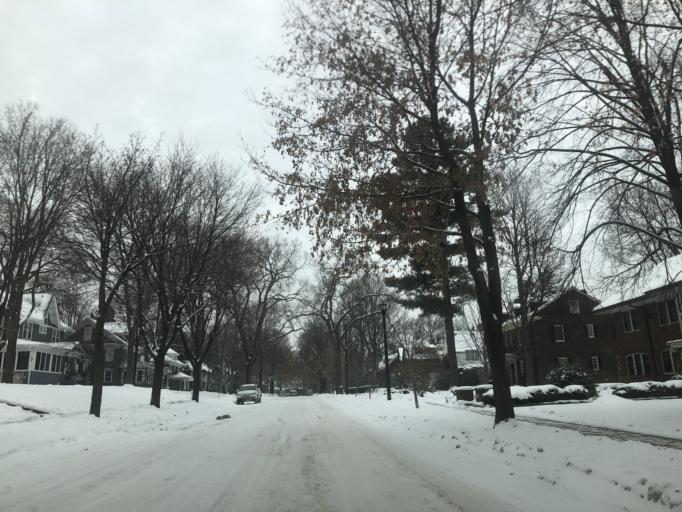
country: US
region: Minnesota
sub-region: Hennepin County
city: Richfield
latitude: 44.9227
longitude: -93.2951
